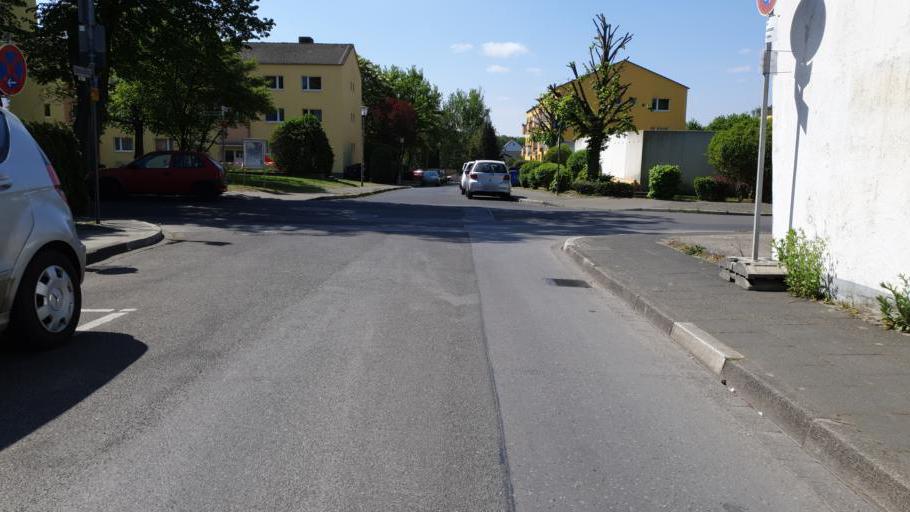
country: DE
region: North Rhine-Westphalia
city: Opladen
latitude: 51.0422
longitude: 7.0463
